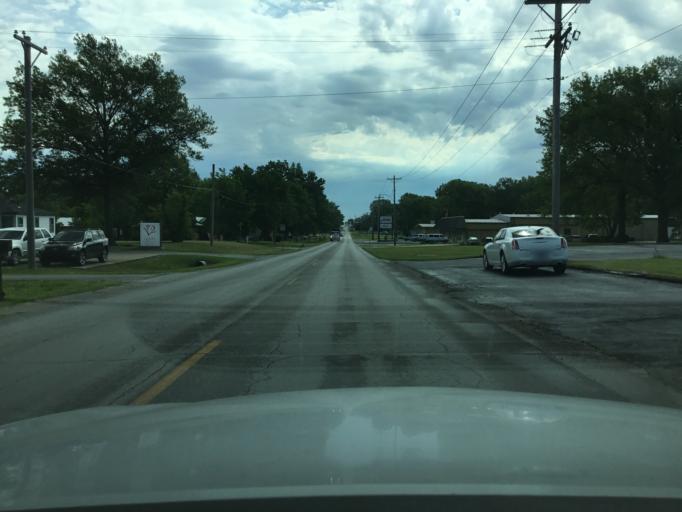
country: US
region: Kansas
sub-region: Montgomery County
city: Coffeyville
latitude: 37.0363
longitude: -95.6530
